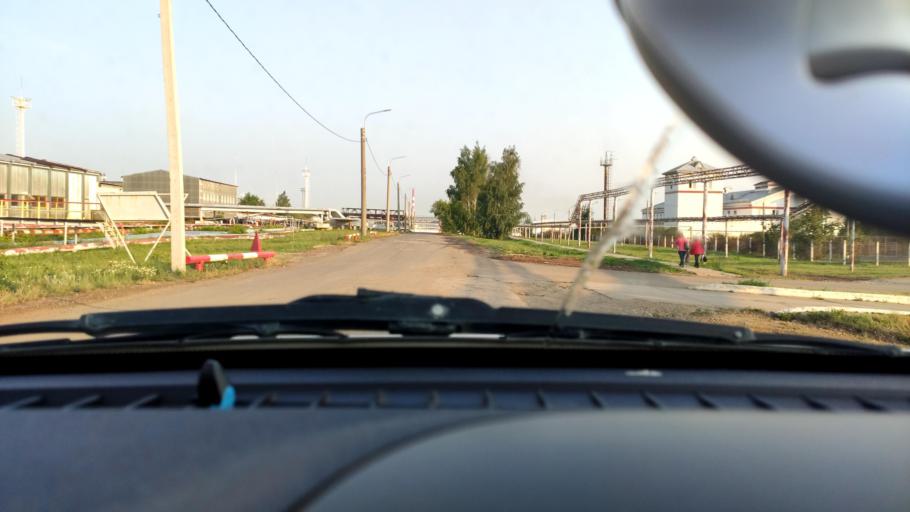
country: RU
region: Perm
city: Gamovo
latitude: 57.9082
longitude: 56.1498
